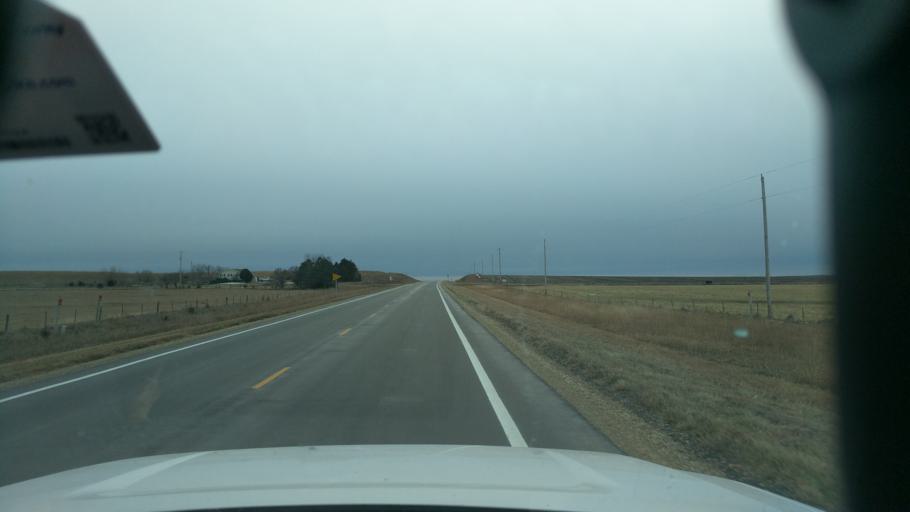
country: US
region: Kansas
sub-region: Dickinson County
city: Herington
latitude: 38.7416
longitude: -96.9276
